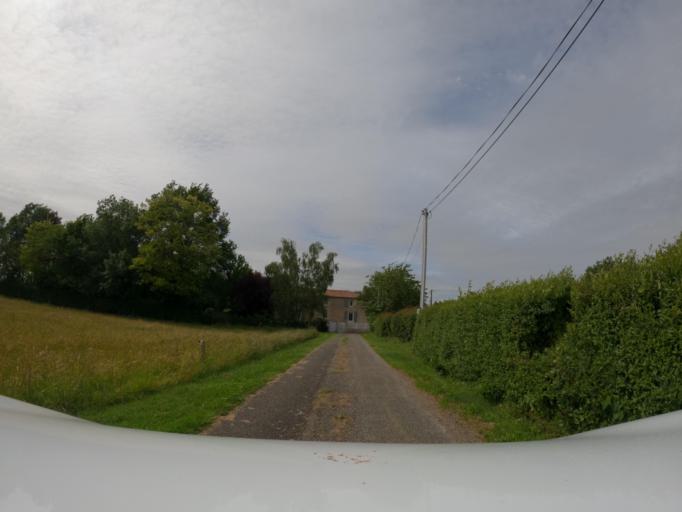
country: FR
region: Pays de la Loire
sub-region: Departement de la Vendee
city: Saint-Hilaire-des-Loges
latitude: 46.4973
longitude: -0.6575
